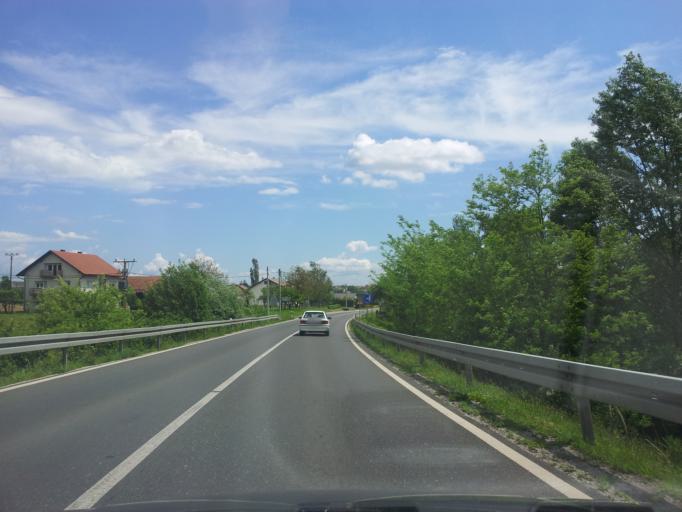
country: HR
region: Zagrebacka
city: Jastrebarsko
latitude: 45.6895
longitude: 15.7179
